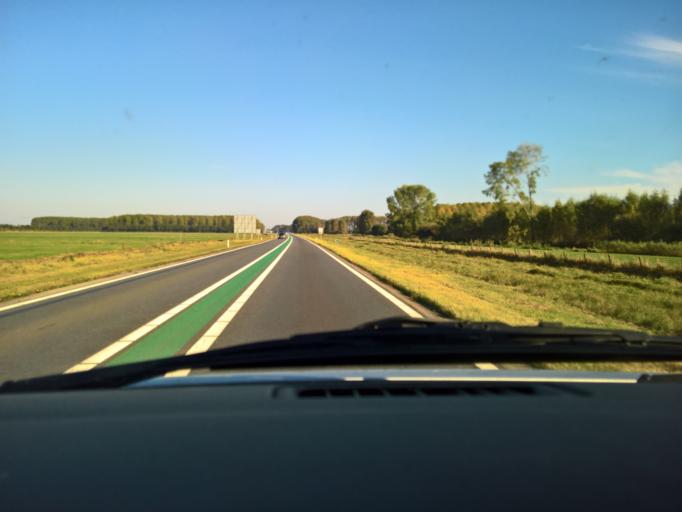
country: NL
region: Gelderland
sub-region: Gemeente Druten
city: Druten
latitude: 51.8678
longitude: 5.5907
